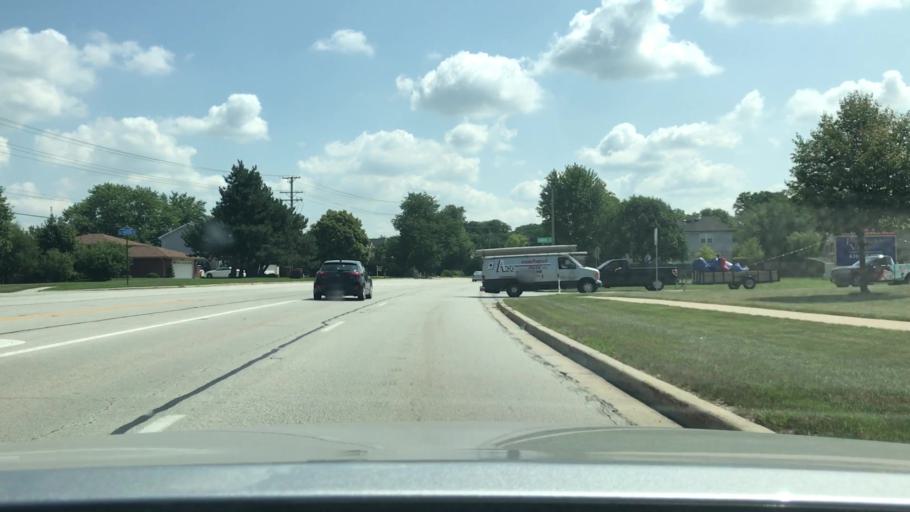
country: US
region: Illinois
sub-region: DuPage County
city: Woodridge
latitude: 41.7288
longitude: -88.0243
